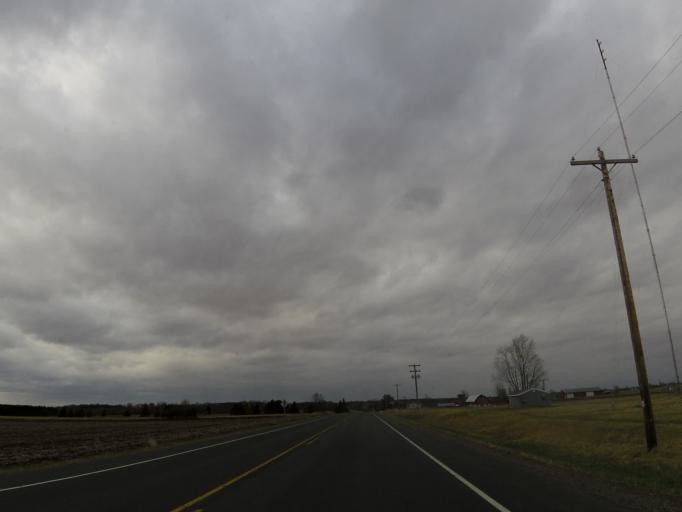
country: US
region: Wisconsin
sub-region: Saint Croix County
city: New Richmond
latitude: 45.0845
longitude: -92.5730
